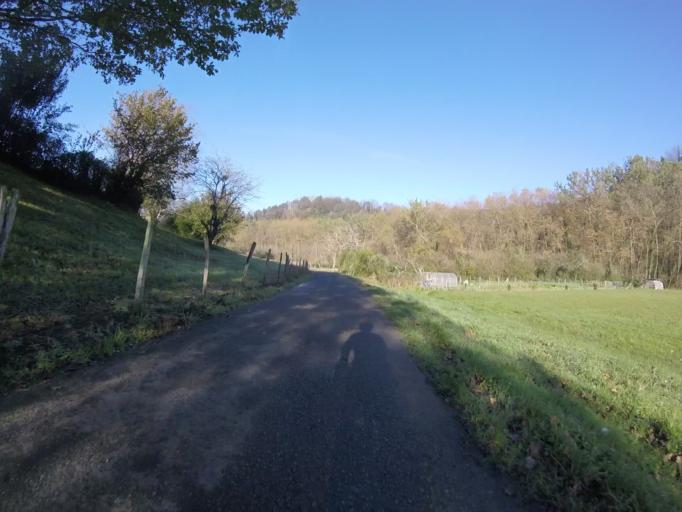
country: ES
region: Basque Country
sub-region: Provincia de Guipuzcoa
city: Usurbil
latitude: 43.2769
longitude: -2.0605
